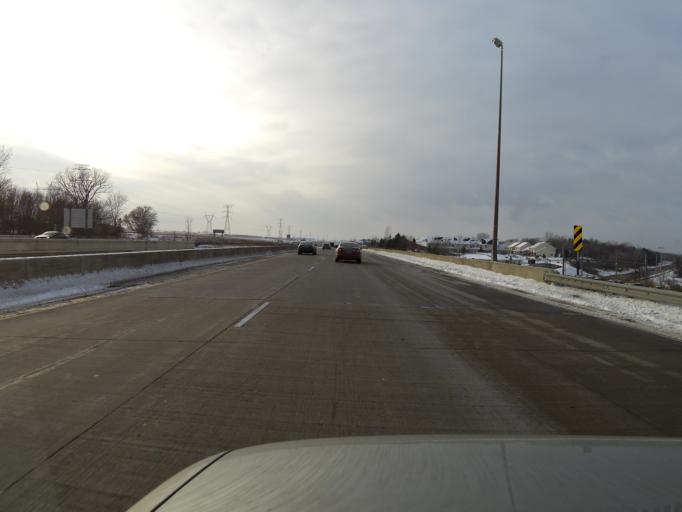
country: US
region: Minnesota
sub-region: Scott County
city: Shakopee
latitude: 44.7814
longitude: -93.4761
